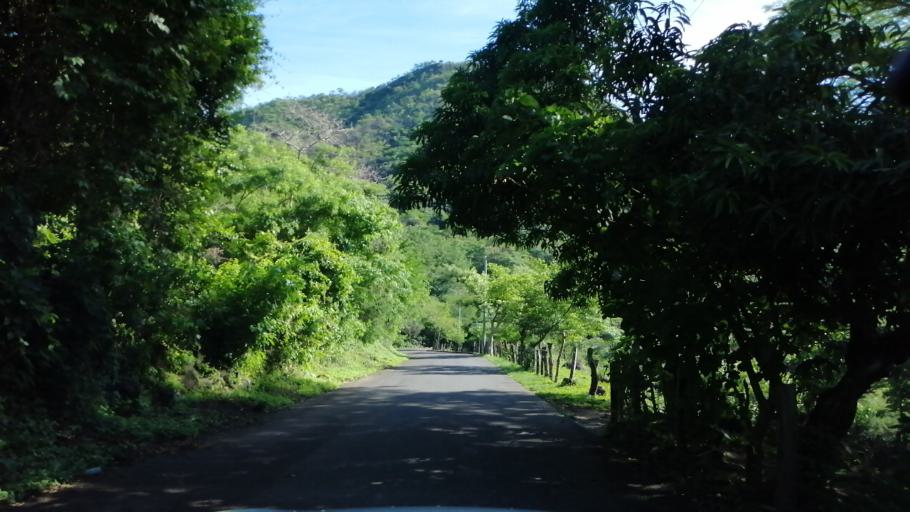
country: SV
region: Morazan
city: Corinto
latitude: 13.7934
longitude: -88.0124
